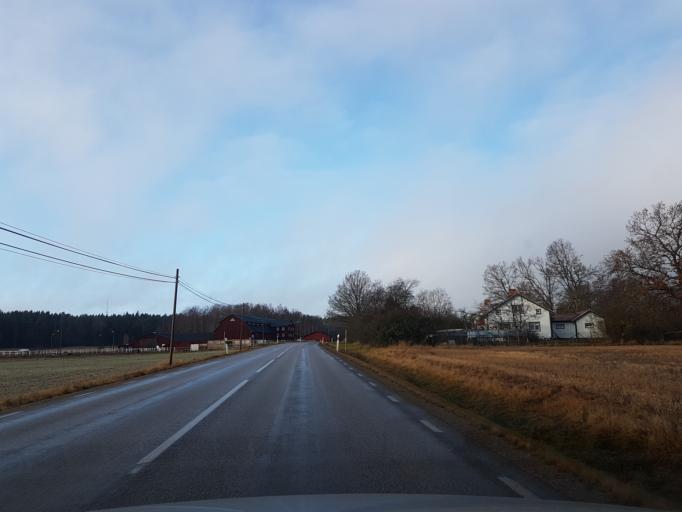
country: SE
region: Stockholm
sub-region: Nykvarns Kommun
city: Nykvarn
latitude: 59.2044
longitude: 17.4030
